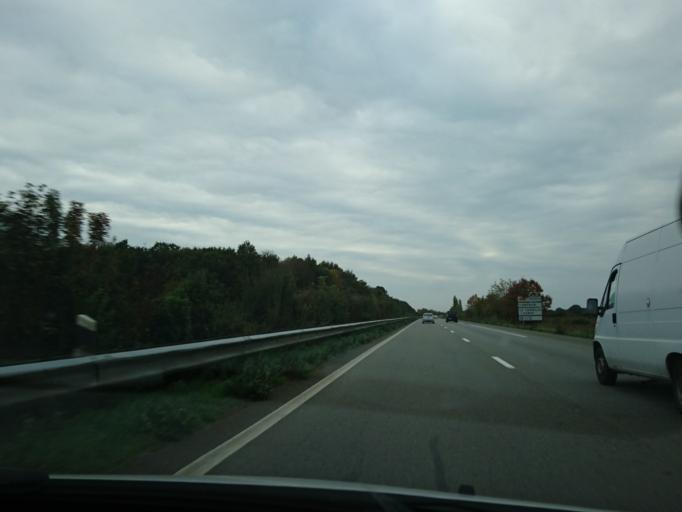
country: FR
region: Pays de la Loire
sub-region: Departement de la Loire-Atlantique
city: Savenay
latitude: 47.3770
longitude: -1.9481
